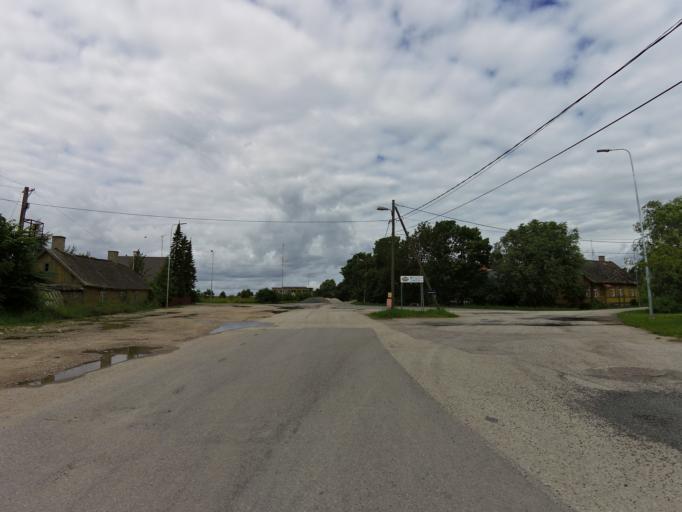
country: EE
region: Laeaene
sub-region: Haapsalu linn
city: Haapsalu
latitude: 58.9564
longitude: 23.5251
